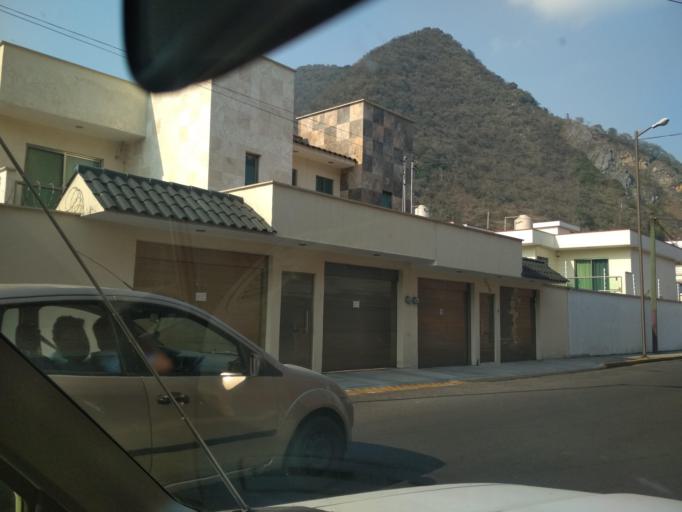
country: MX
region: Veracruz
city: Orizaba
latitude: 18.8565
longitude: -97.0905
